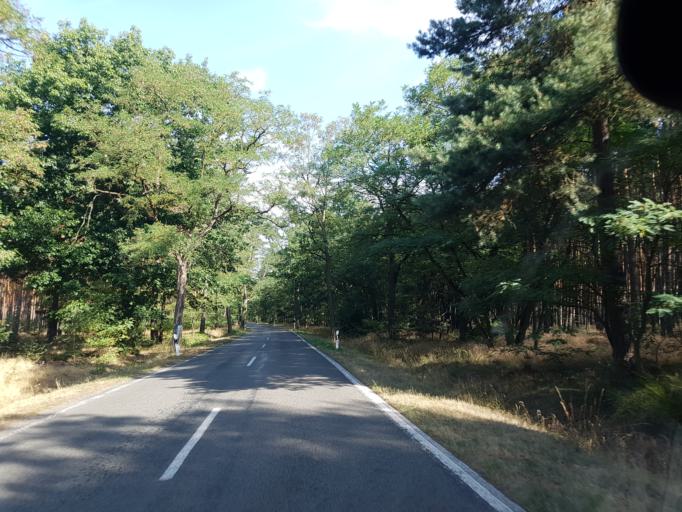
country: DE
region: Brandenburg
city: Ihlow
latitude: 51.9661
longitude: 13.3183
